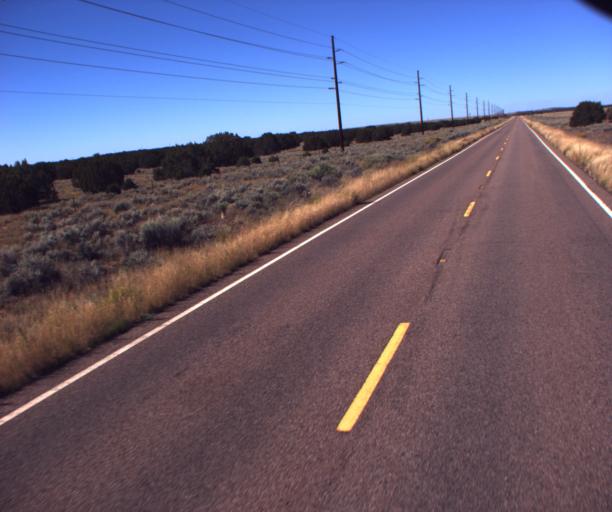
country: US
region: Arizona
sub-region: Navajo County
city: Taylor
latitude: 34.4832
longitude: -110.2734
